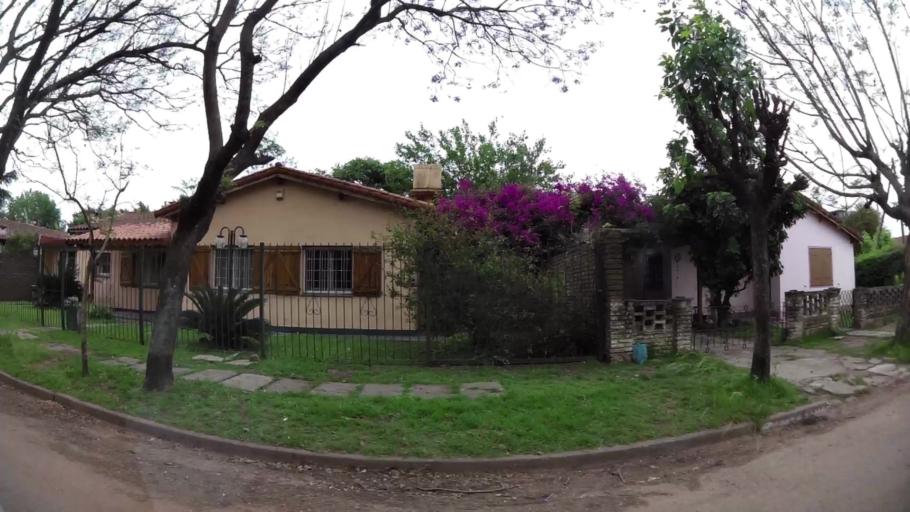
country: AR
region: Buenos Aires
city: San Justo
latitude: -34.7119
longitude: -58.5378
